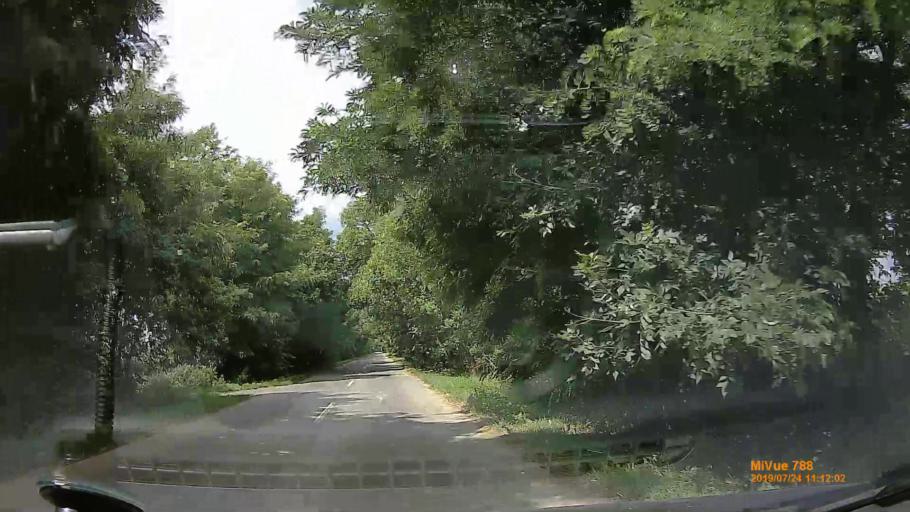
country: HU
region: Szabolcs-Szatmar-Bereg
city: Tarpa
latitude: 48.2031
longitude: 22.4617
